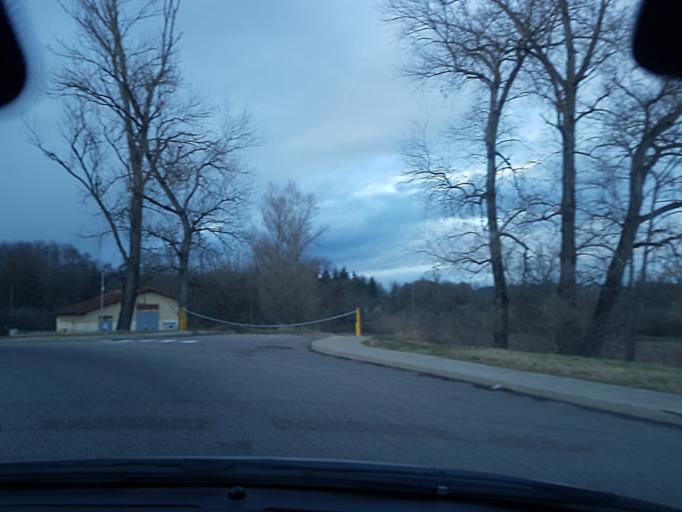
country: FR
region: Rhone-Alpes
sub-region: Departement du Rhone
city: Montagny
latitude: 45.6401
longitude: 4.7558
